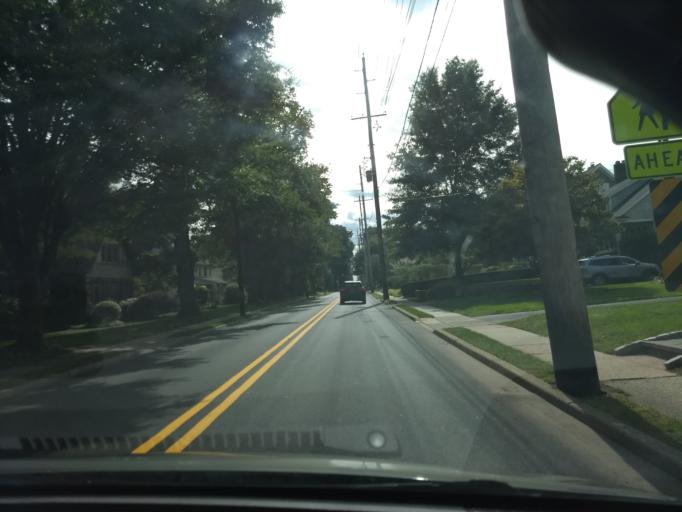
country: US
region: New Jersey
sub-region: Bergen County
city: Glen Rock
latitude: 40.9672
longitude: -74.1216
